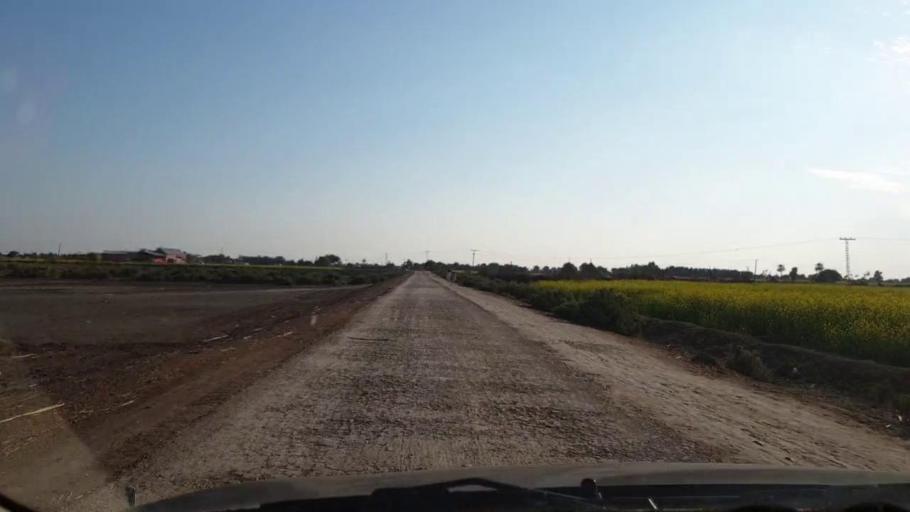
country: PK
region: Sindh
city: Jhol
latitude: 25.9560
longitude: 68.8615
